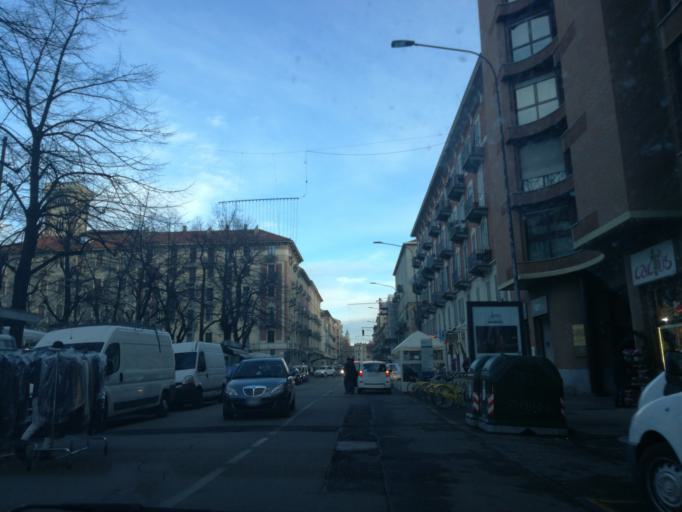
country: IT
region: Piedmont
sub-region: Provincia di Torino
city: Turin
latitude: 45.0732
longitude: 7.6622
